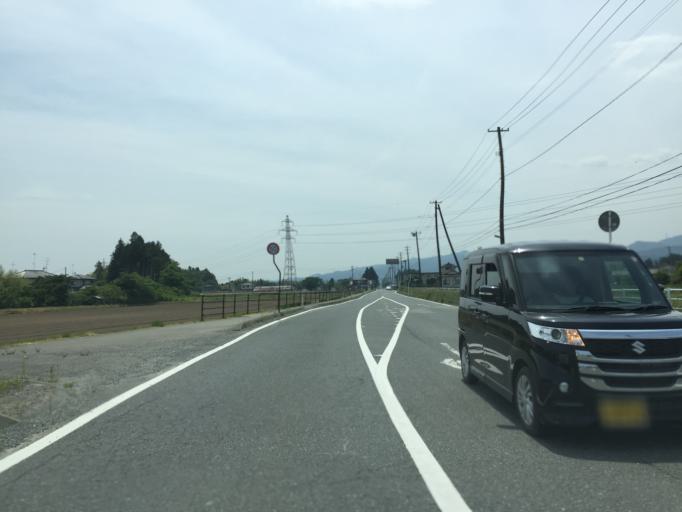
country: JP
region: Fukushima
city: Namie
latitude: 37.6262
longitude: 140.9365
